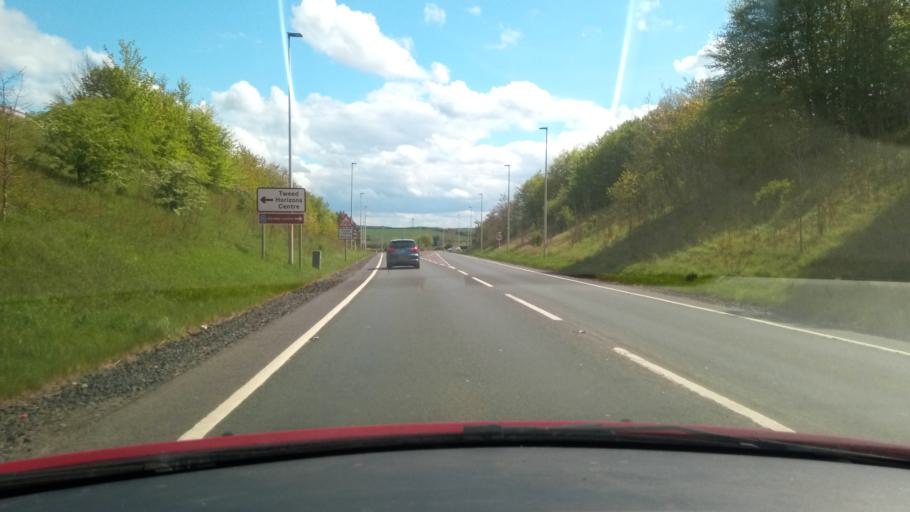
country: GB
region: Scotland
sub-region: The Scottish Borders
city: Newtown St Boswells
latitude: 55.5764
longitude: -2.6650
